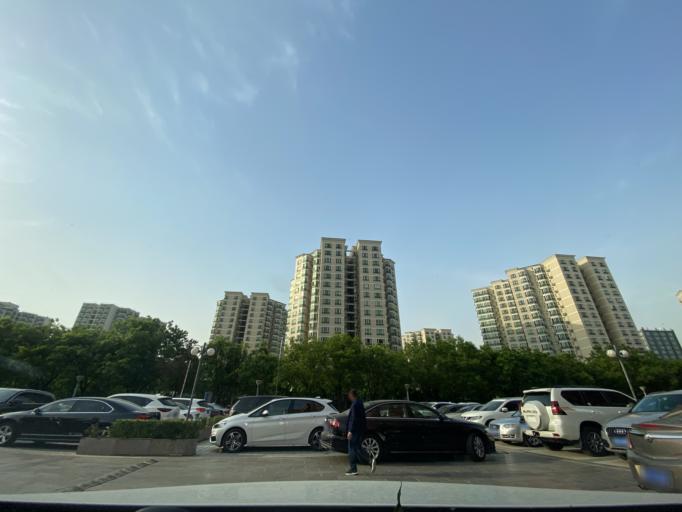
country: CN
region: Beijing
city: Sijiqing
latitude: 39.9579
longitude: 116.2789
